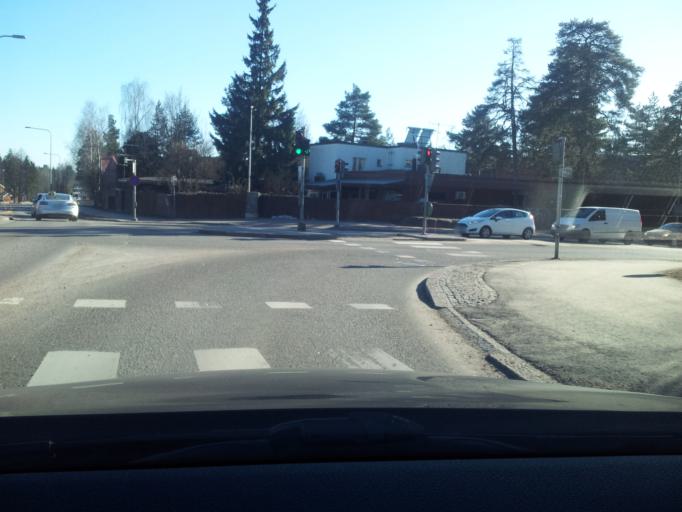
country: FI
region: Uusimaa
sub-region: Helsinki
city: Kauniainen
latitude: 60.1735
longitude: 24.7295
